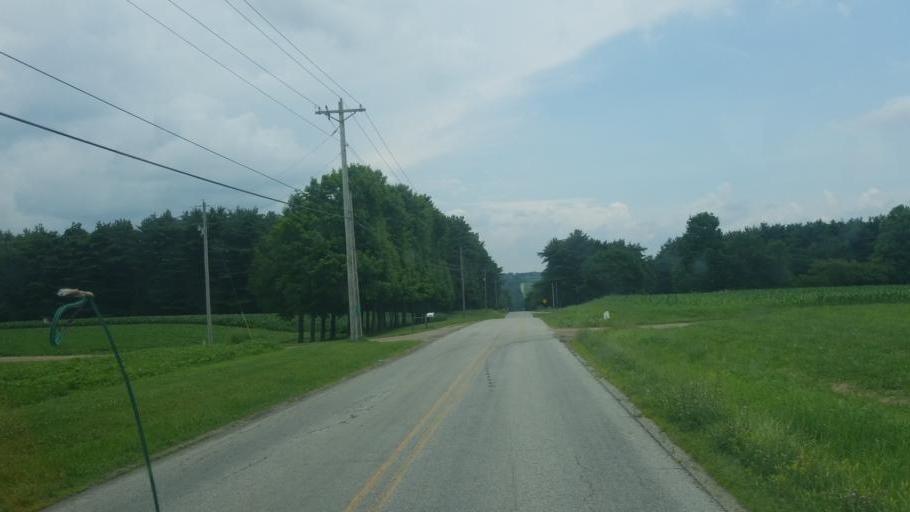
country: US
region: Ohio
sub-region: Wayne County
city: Wooster
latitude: 40.8580
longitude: -82.0213
